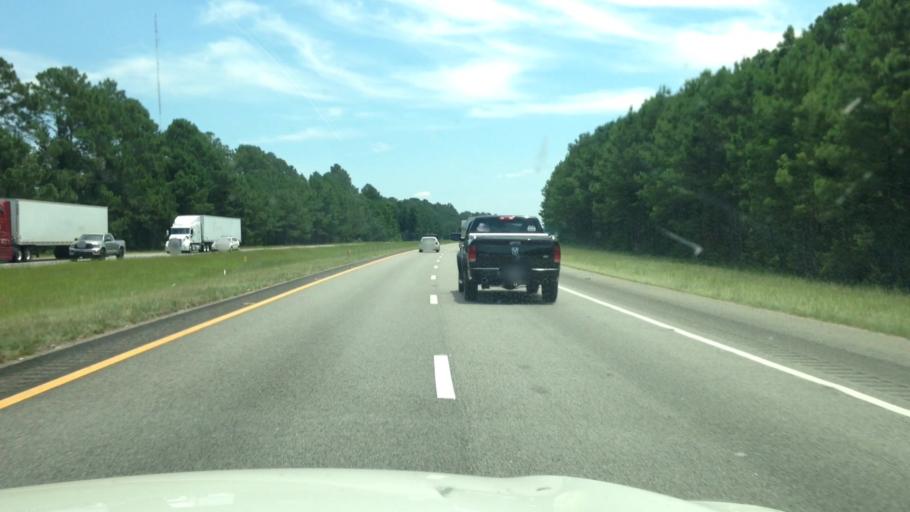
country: US
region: South Carolina
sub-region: Darlington County
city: Darlington
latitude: 34.2038
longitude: -79.8713
